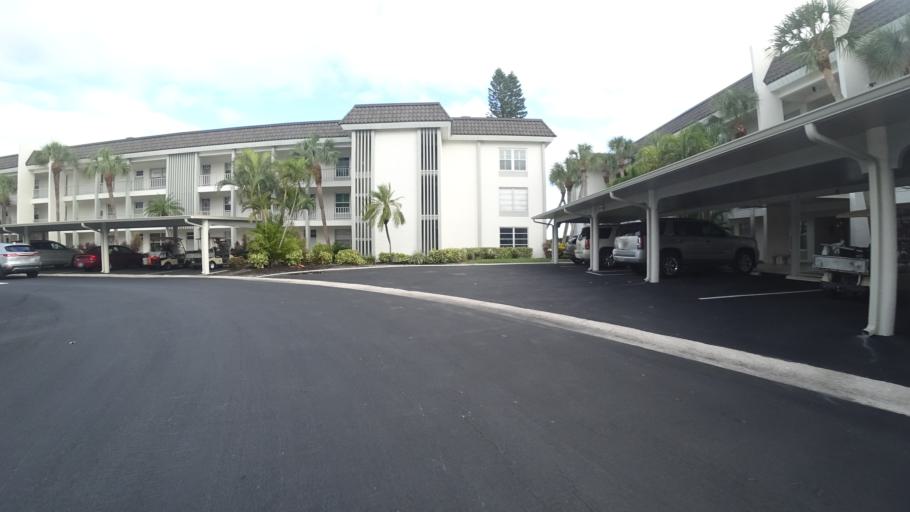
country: US
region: Florida
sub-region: Manatee County
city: Longboat Key
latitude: 27.3955
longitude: -82.6430
